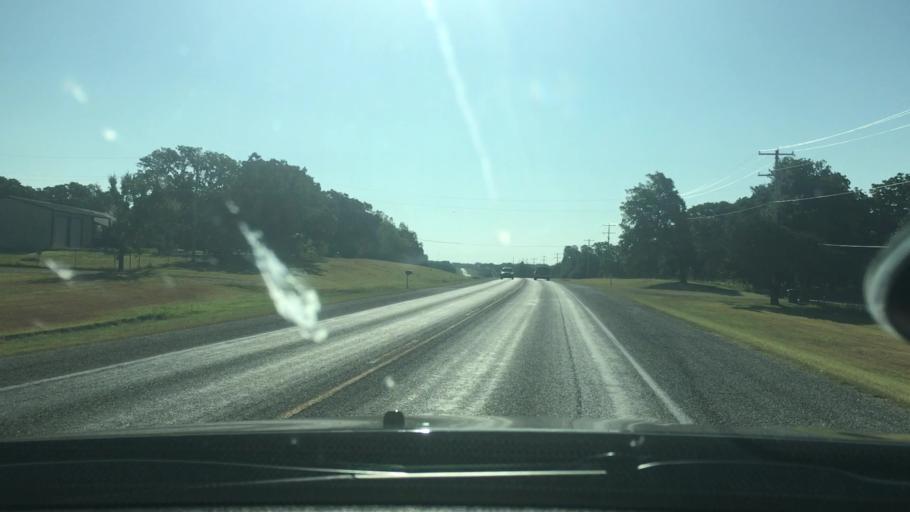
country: US
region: Oklahoma
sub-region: Johnston County
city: Tishomingo
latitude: 34.2369
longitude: -96.7277
